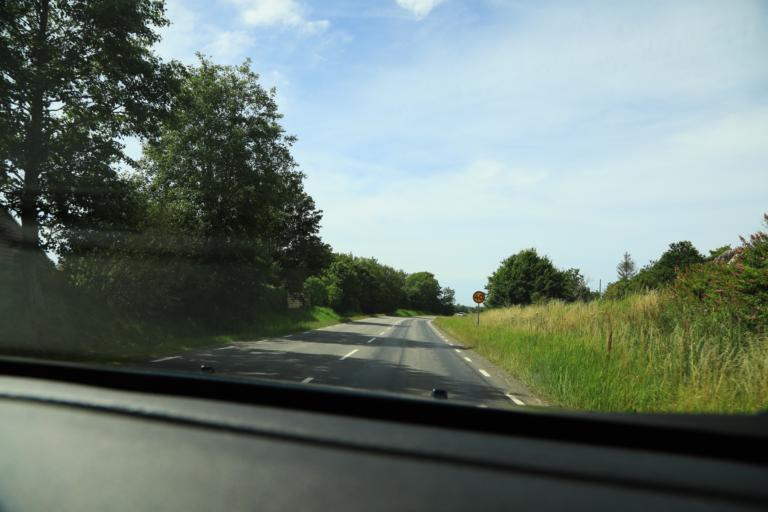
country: SE
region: Halland
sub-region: Varbergs Kommun
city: Varberg
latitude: 57.1416
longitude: 12.2848
